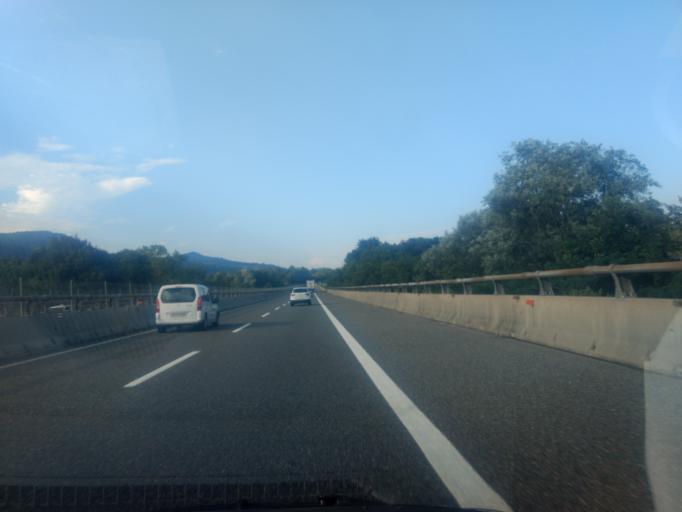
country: IT
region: Piedmont
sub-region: Provincia di Novara
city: Pisano
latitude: 45.7847
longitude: 8.5119
